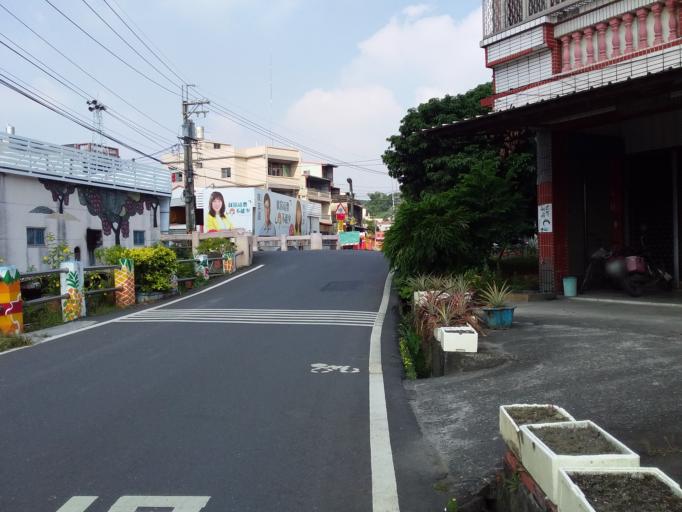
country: TW
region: Taiwan
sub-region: Pingtung
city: Pingtung
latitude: 22.6878
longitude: 120.4125
